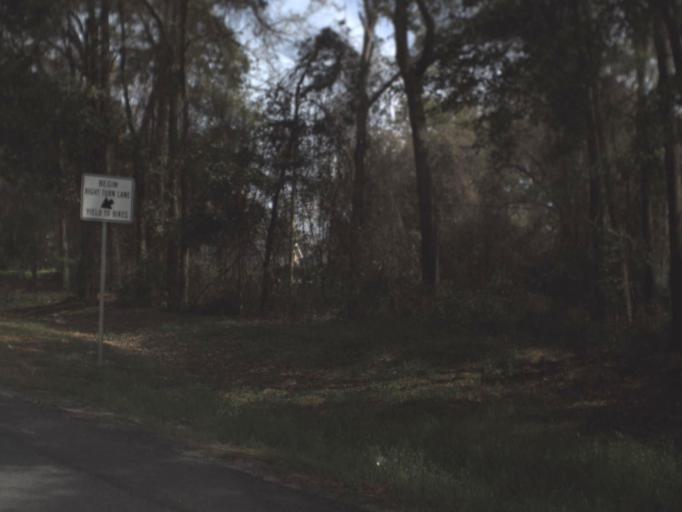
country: US
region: Florida
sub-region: Gadsden County
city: Midway
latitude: 30.5242
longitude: -84.3635
